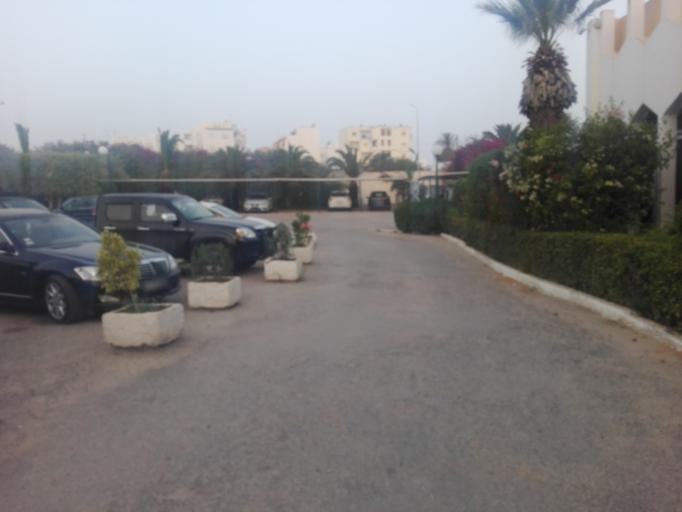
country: TN
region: Safaqis
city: Sfax
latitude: 34.7327
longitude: 10.7401
